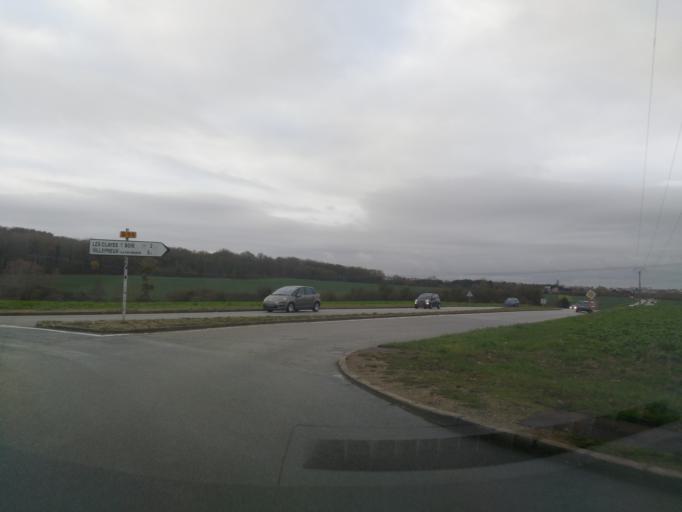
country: FR
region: Ile-de-France
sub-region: Departement des Yvelines
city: Bois-d'Arcy
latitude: 48.8177
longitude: 2.0247
